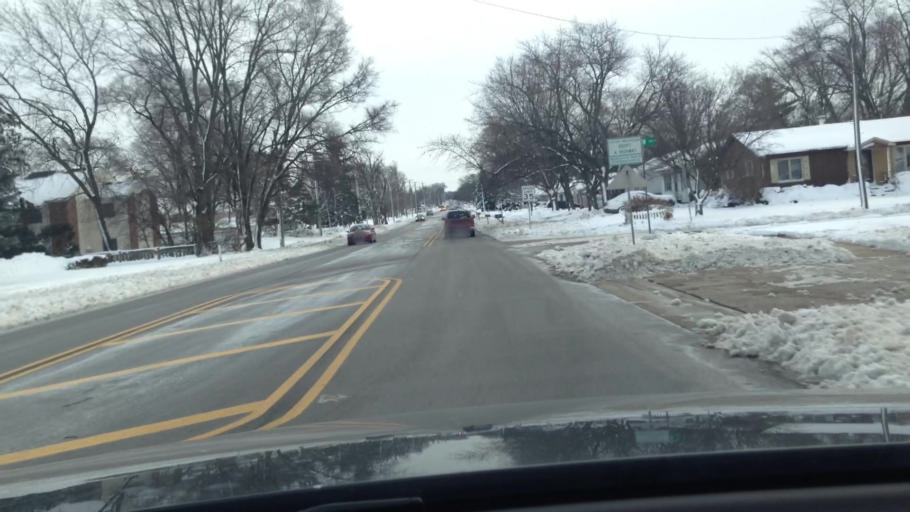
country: US
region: Illinois
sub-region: McHenry County
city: Woodstock
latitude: 42.3327
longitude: -88.4432
